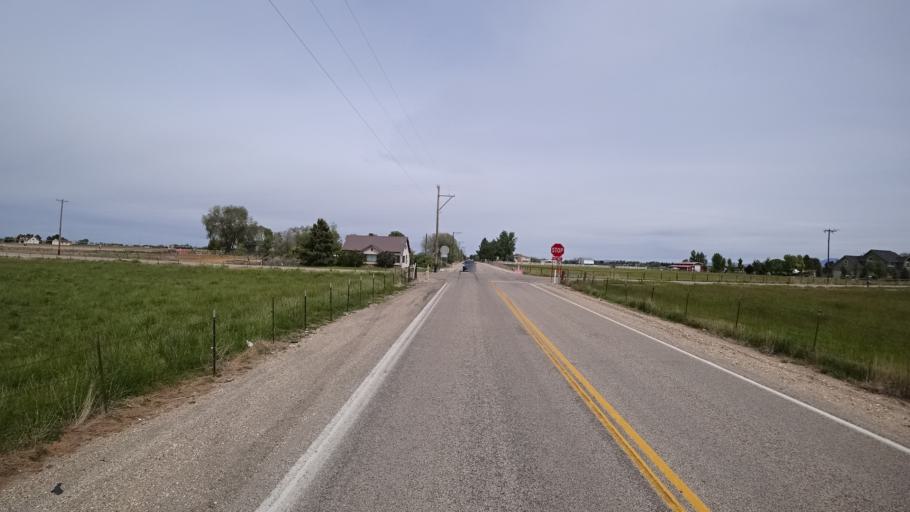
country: US
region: Idaho
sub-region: Ada County
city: Kuna
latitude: 43.5464
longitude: -116.4737
